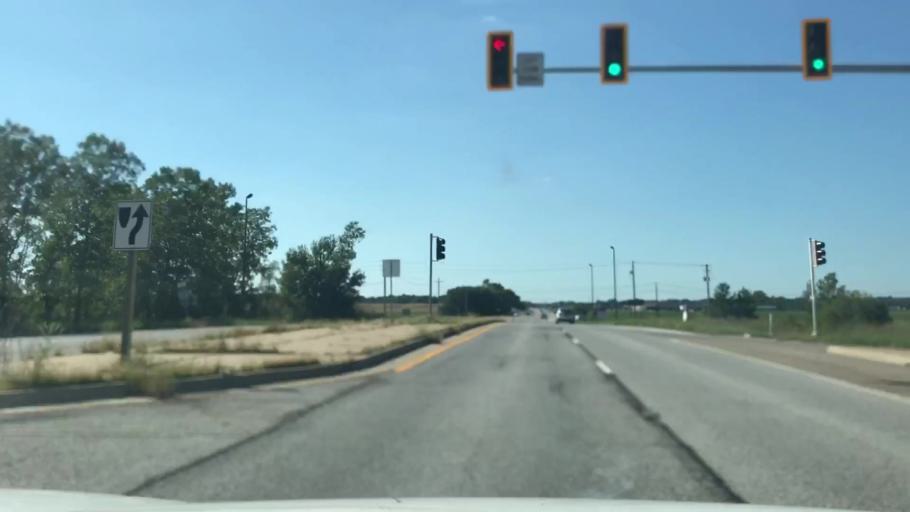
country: US
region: Illinois
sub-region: Madison County
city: Roxana
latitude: 38.8514
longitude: -90.0537
